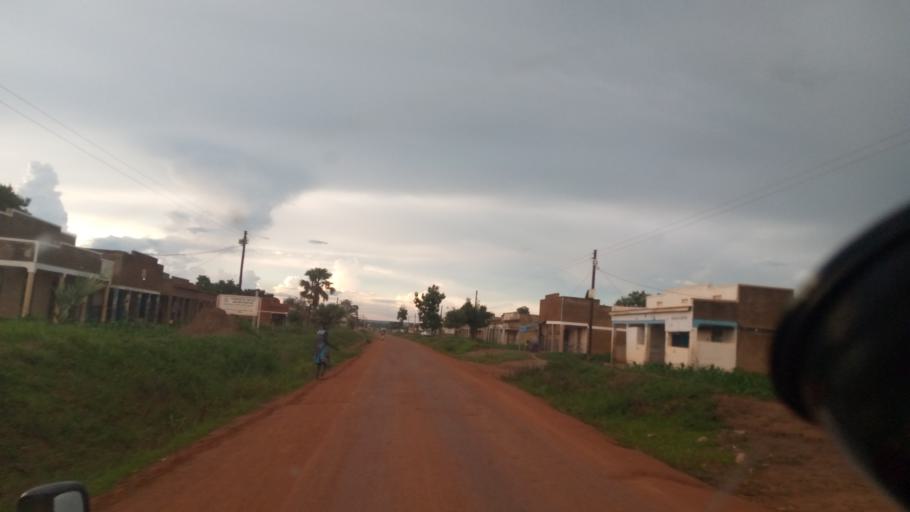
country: UG
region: Northern Region
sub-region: Kole District
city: Kole
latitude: 2.4829
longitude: 32.9358
